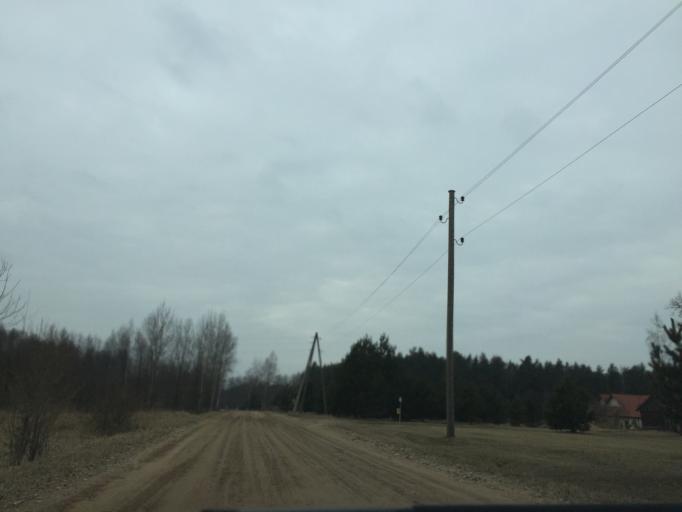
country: LV
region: Kekava
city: Balozi
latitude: 56.7920
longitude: 24.1465
